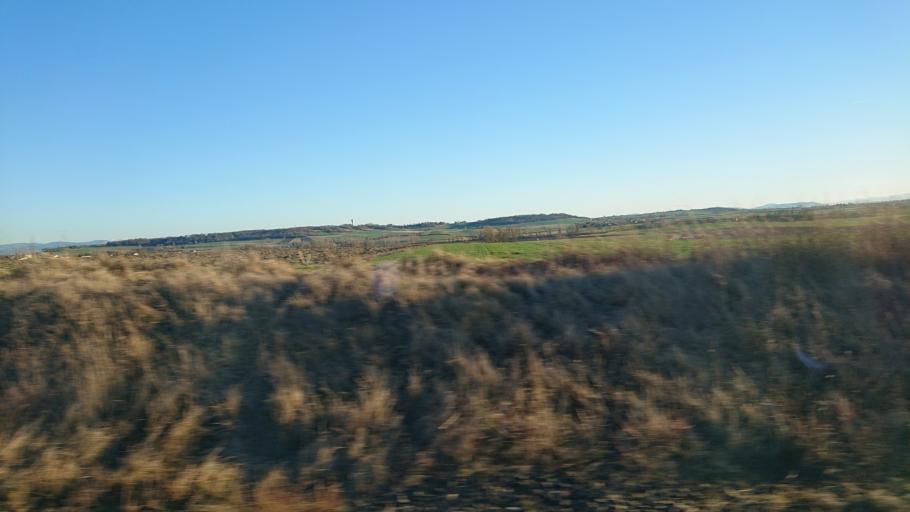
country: FR
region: Auvergne
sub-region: Departement du Puy-de-Dome
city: Randan
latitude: 46.0045
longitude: 3.3363
